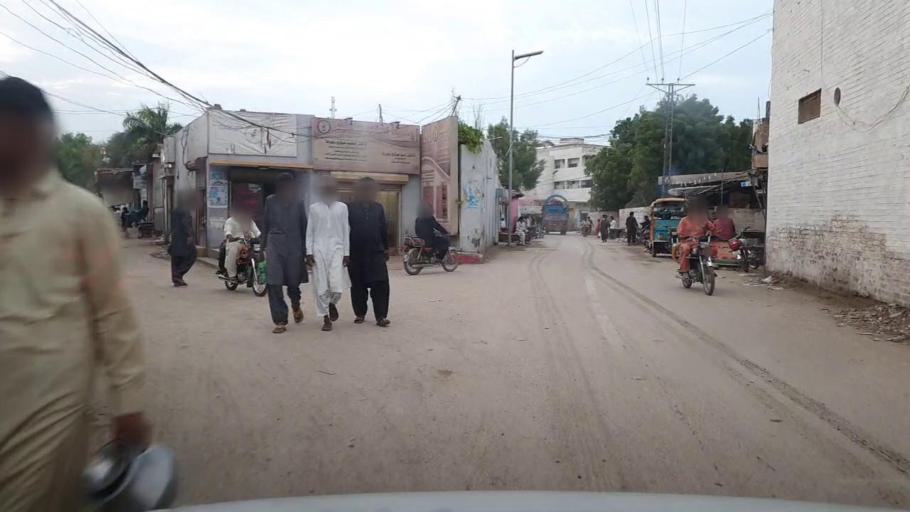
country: PK
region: Sindh
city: Naushahro Firoz
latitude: 26.8371
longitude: 68.1230
